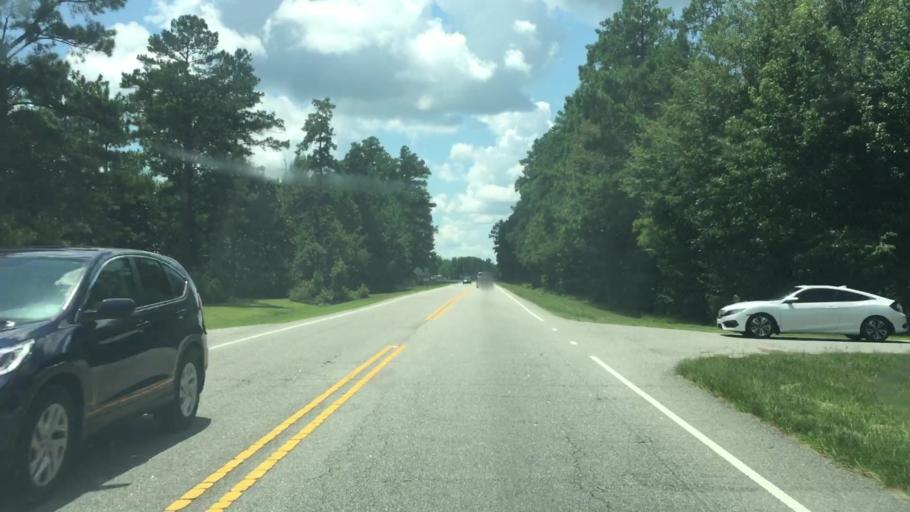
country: US
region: North Carolina
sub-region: Columbus County
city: Tabor City
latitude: 34.1388
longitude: -78.8707
